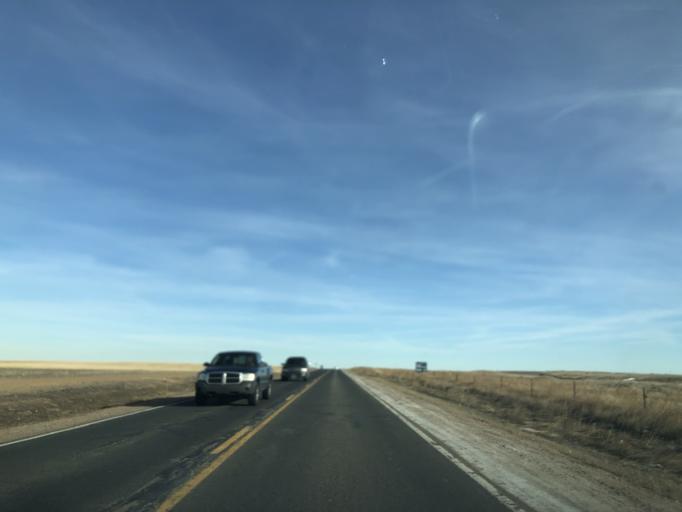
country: US
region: Colorado
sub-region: Adams County
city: Aurora
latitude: 39.7984
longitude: -104.7313
